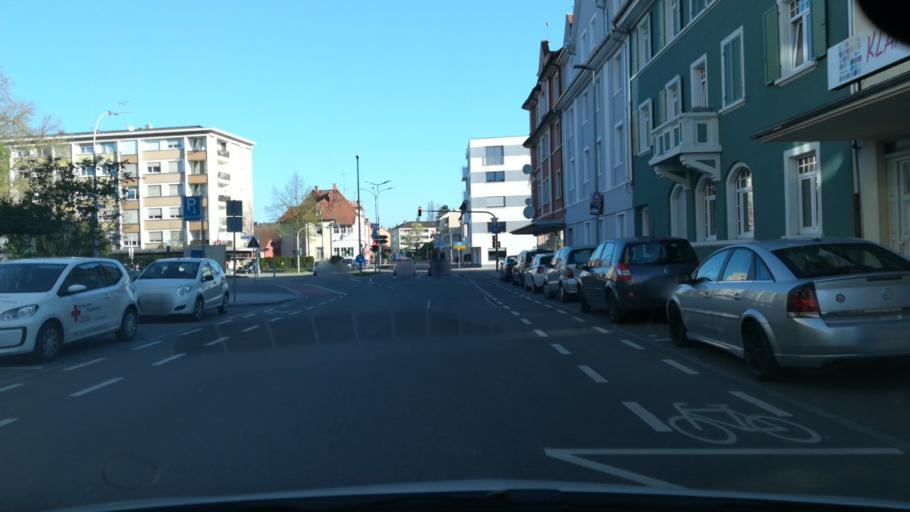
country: DE
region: Baden-Wuerttemberg
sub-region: Freiburg Region
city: Singen
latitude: 47.7628
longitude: 8.8454
